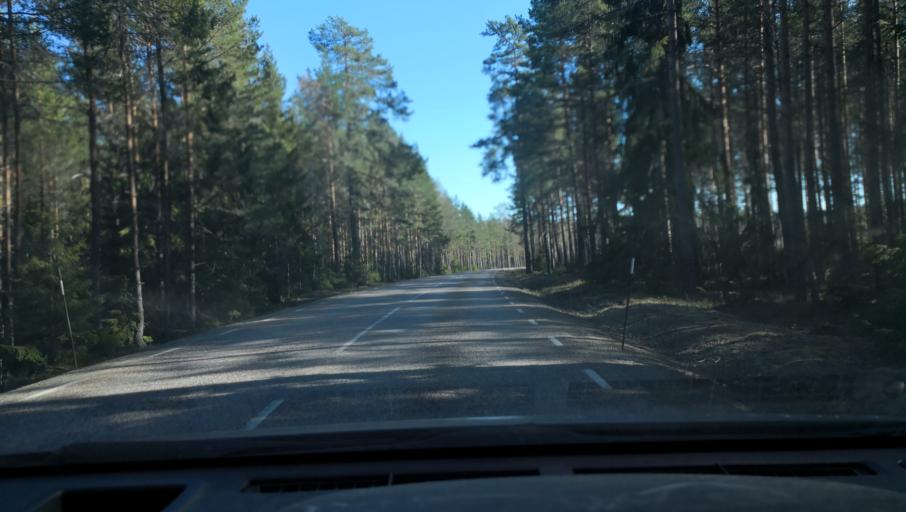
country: SE
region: Dalarna
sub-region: Avesta Kommun
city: Avesta
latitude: 59.9820
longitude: 16.3362
